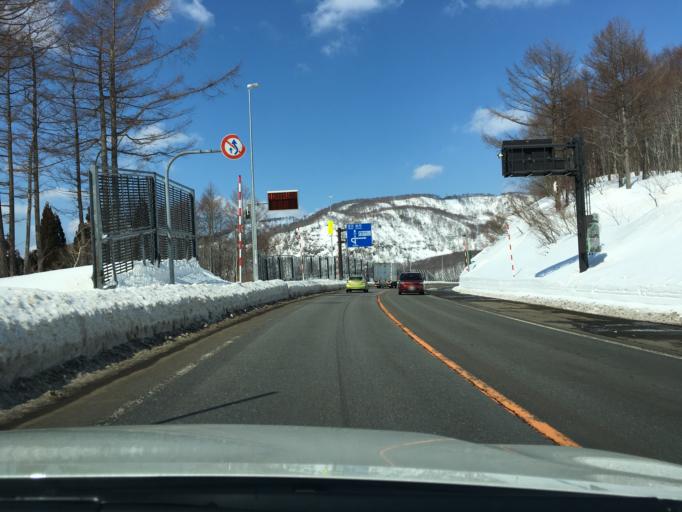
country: JP
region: Yamagata
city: Tsuruoka
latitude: 38.5247
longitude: 139.9492
